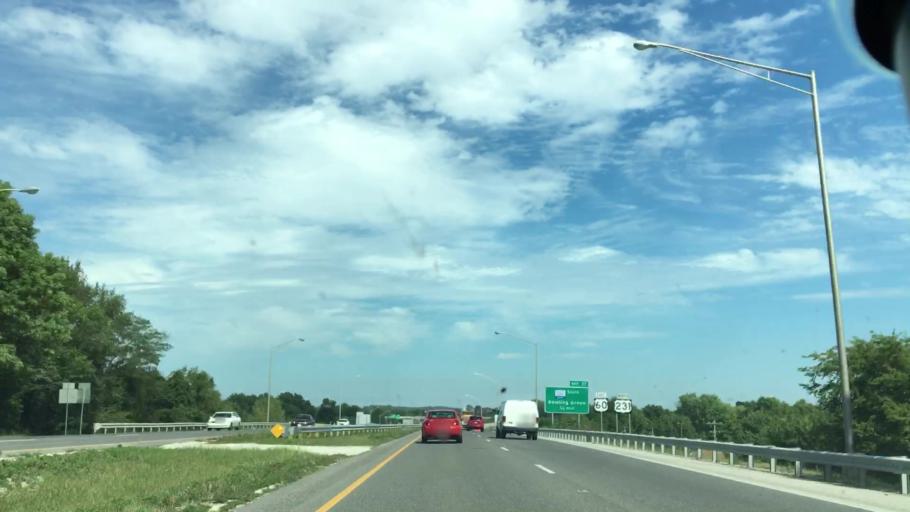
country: US
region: Kentucky
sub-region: Daviess County
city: Owensboro
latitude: 37.7350
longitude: -87.0820
